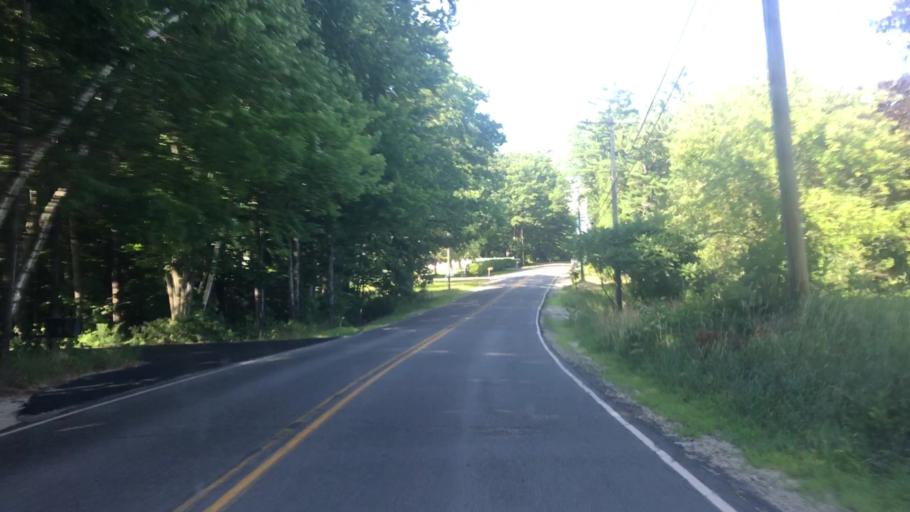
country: US
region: Maine
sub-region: York County
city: Buxton
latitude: 43.7224
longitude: -70.5646
